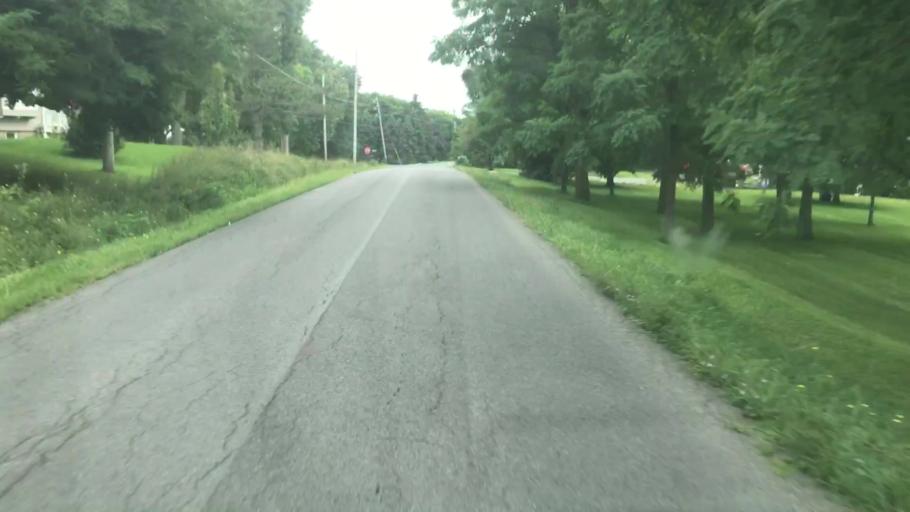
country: US
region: New York
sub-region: Onondaga County
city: Skaneateles
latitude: 42.9562
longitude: -76.4563
